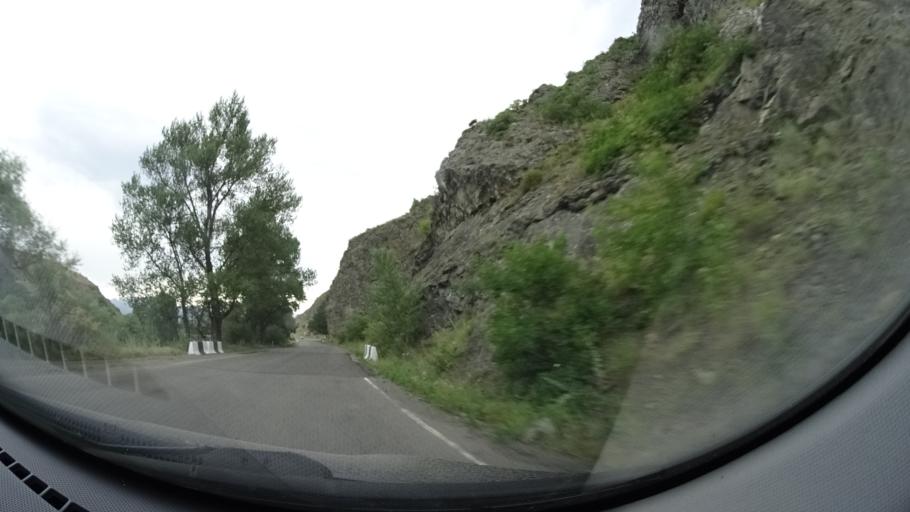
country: GE
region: Samtskhe-Javakheti
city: Akhaltsikhe
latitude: 41.6239
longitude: 43.0502
